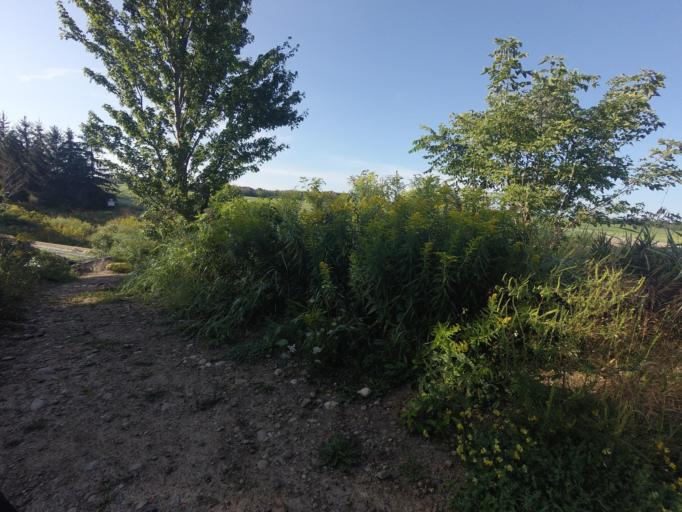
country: CA
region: Ontario
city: Goderich
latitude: 43.7589
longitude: -81.5191
